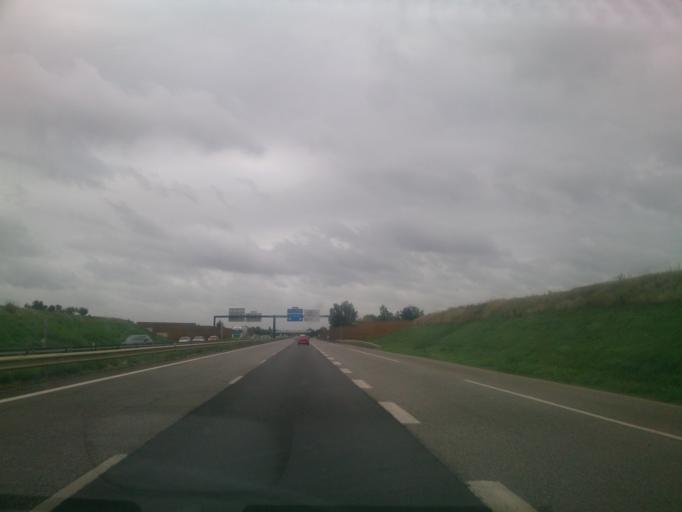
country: FR
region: Midi-Pyrenees
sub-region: Departement de la Haute-Garonne
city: Seysses
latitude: 43.4706
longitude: 1.3169
